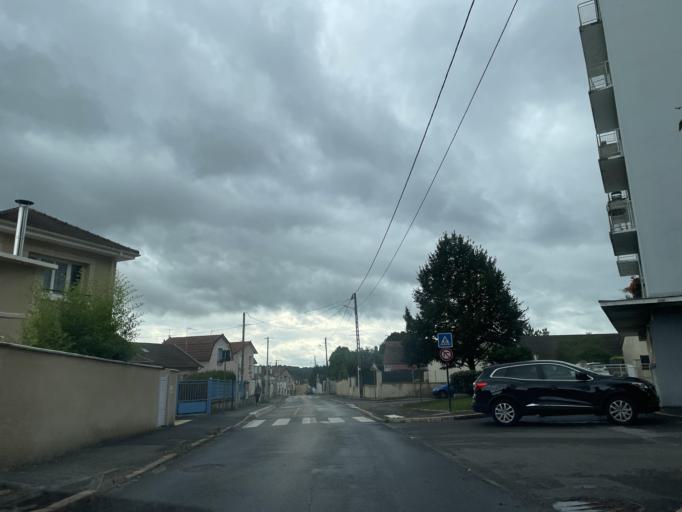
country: FR
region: Ile-de-France
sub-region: Departement de Seine-et-Marne
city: Coulommiers
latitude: 48.8176
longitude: 3.0954
